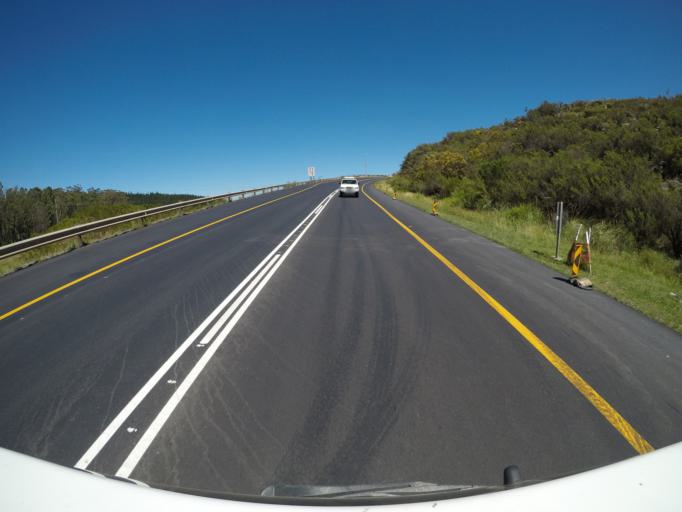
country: ZA
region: Western Cape
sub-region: Overberg District Municipality
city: Grabouw
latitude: -34.1530
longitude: 18.9417
